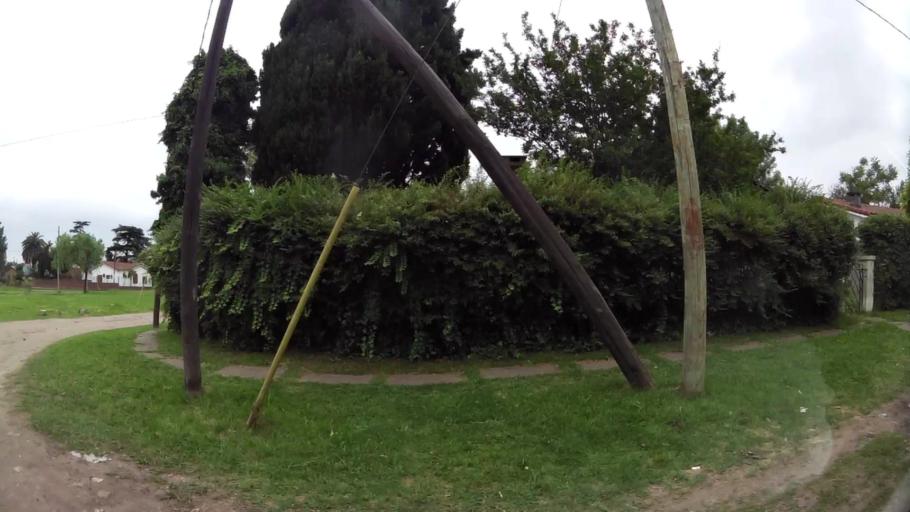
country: AR
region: Buenos Aires
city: San Justo
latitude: -34.7202
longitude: -58.5226
